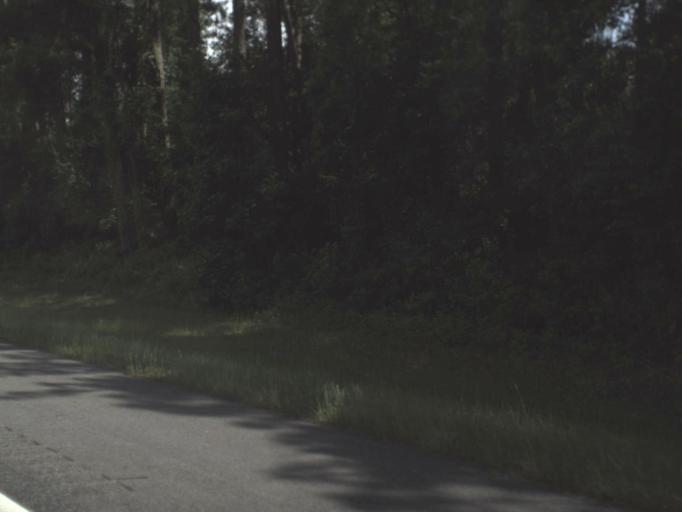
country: US
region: Florida
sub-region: Suwannee County
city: Wellborn
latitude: 30.2613
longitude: -82.7333
